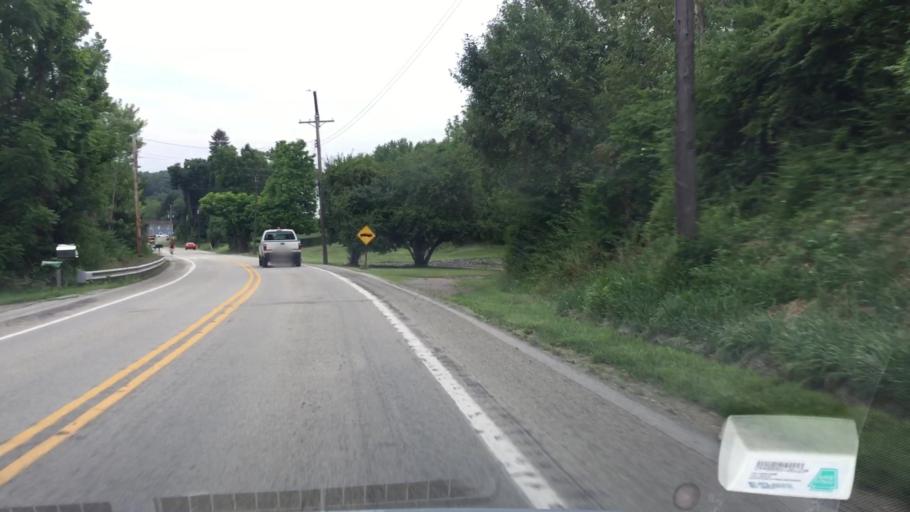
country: US
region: Pennsylvania
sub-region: Allegheny County
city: Curtisville
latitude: 40.6240
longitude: -79.8651
